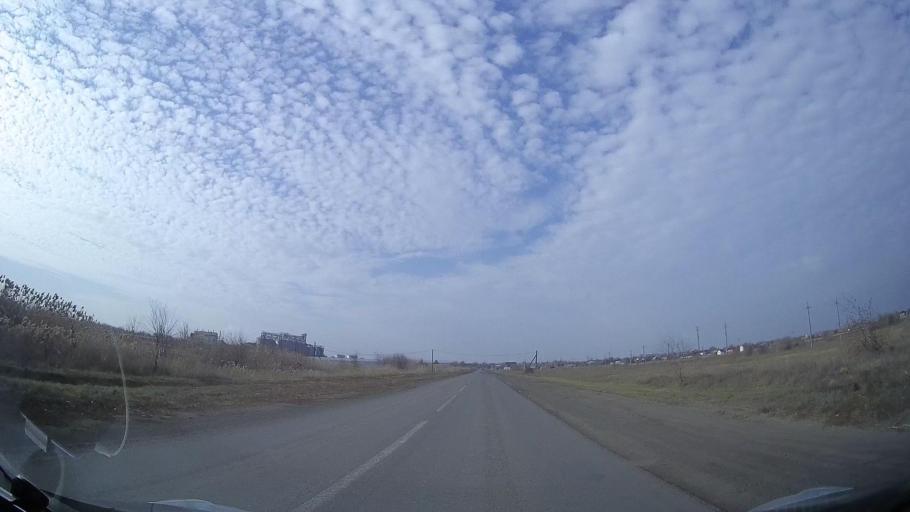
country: RU
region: Rostov
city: Veselyy
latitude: 47.0816
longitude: 40.7755
